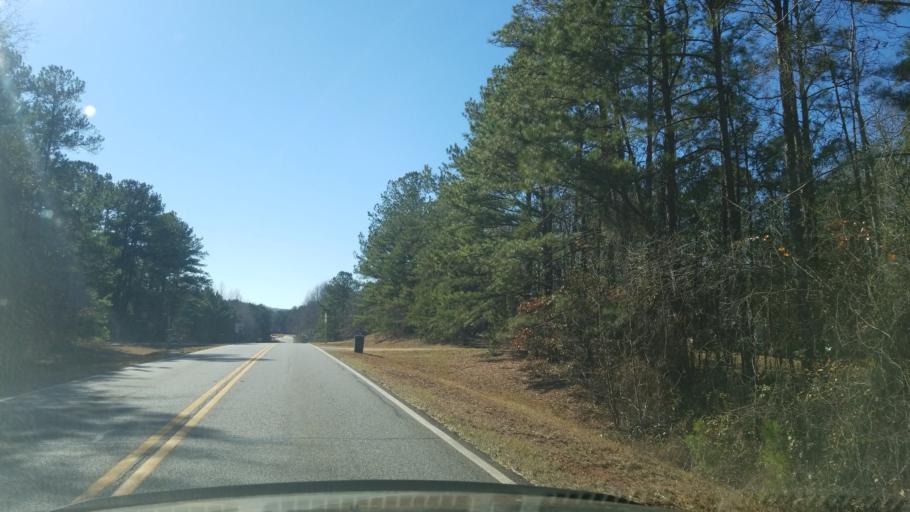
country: US
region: Georgia
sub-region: Talbot County
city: Sardis
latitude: 32.7834
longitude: -84.6868
